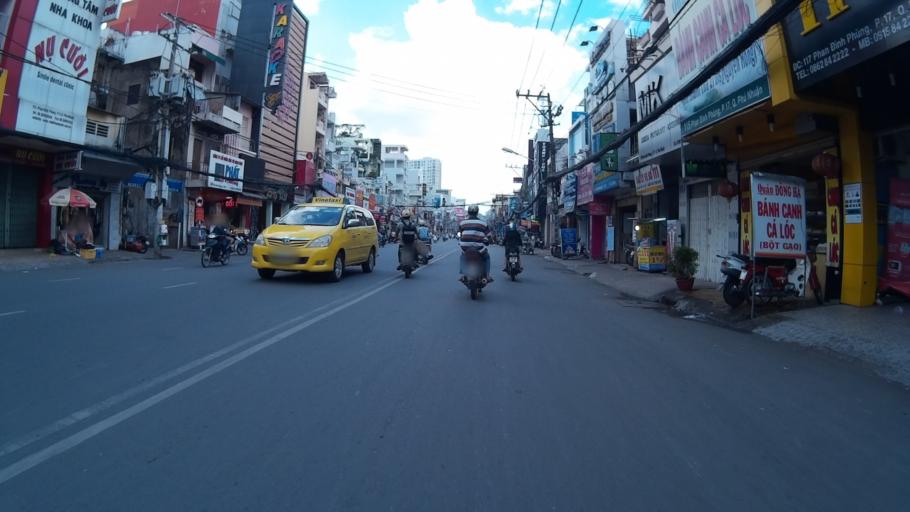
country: VN
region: Ho Chi Minh City
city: Quan Phu Nhuan
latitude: 10.7945
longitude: 106.6835
